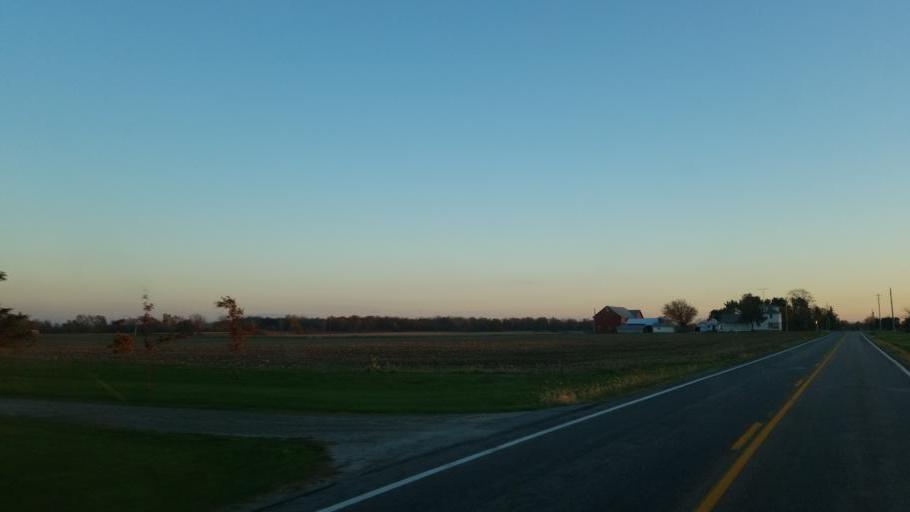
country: US
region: Ohio
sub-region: Huron County
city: Willard
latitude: 41.1178
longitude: -82.7853
